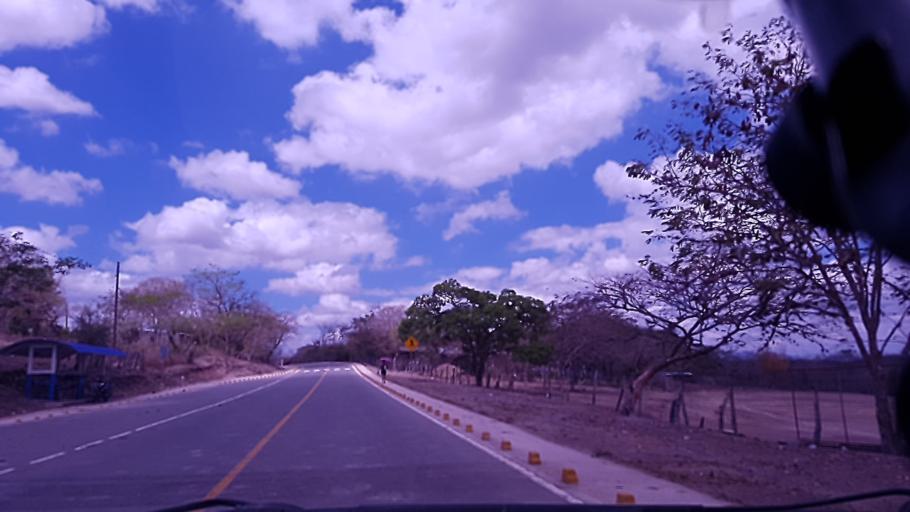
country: NI
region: Esteli
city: Condega
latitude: 13.3770
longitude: -86.3691
